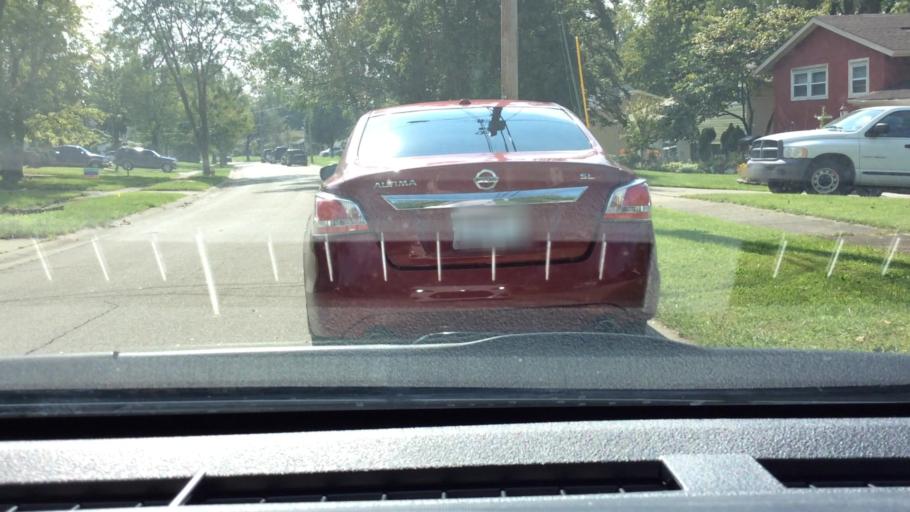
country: US
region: Ohio
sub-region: Hamilton County
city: Greenhills
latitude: 39.2708
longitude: -84.5051
